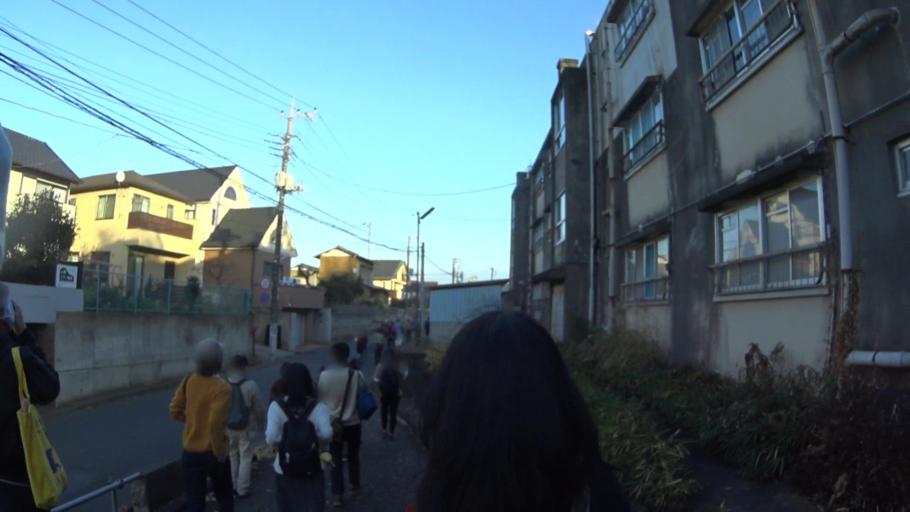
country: JP
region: Ibaraki
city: Mito-shi
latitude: 36.3736
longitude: 140.4614
